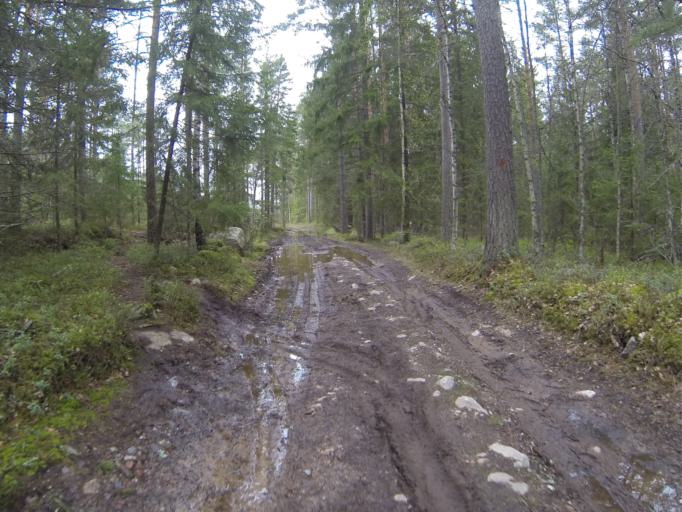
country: FI
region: Varsinais-Suomi
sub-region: Salo
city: Salo
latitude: 60.4028
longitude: 23.2011
